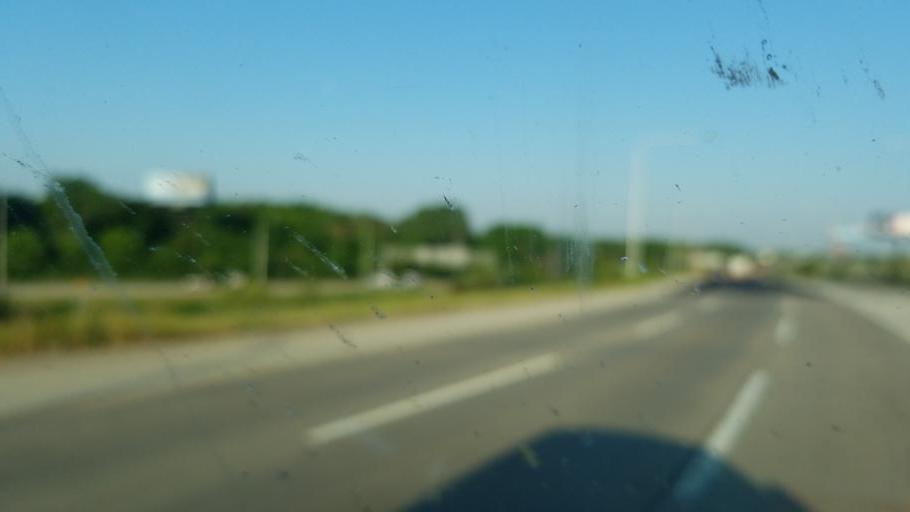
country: US
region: Illinois
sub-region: Cook County
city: University Park
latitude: 41.5837
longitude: -87.6838
